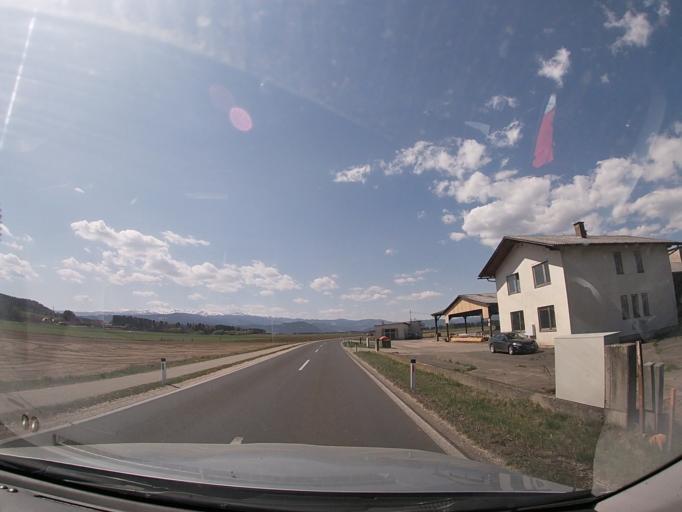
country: AT
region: Styria
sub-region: Politischer Bezirk Murtal
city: Grosslobming
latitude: 47.1813
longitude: 14.7946
